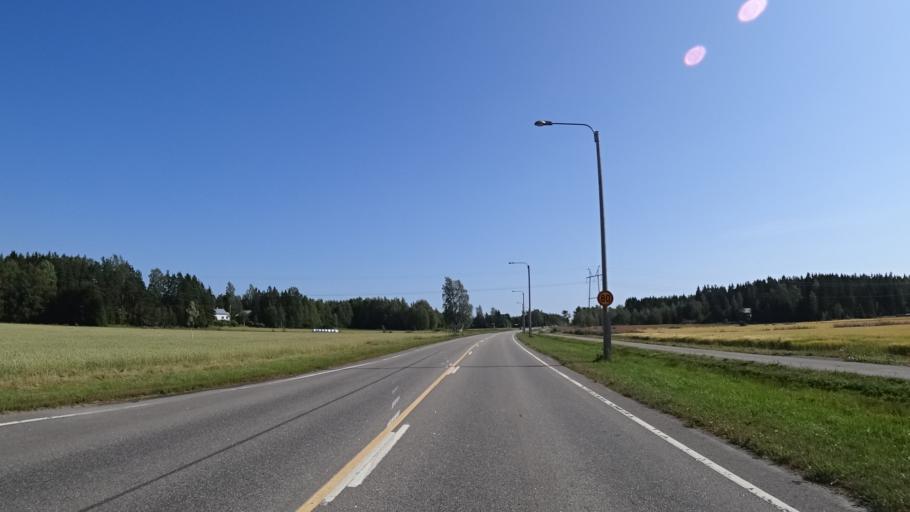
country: FI
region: Kymenlaakso
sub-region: Kotka-Hamina
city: Karhula
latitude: 60.5383
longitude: 26.9317
